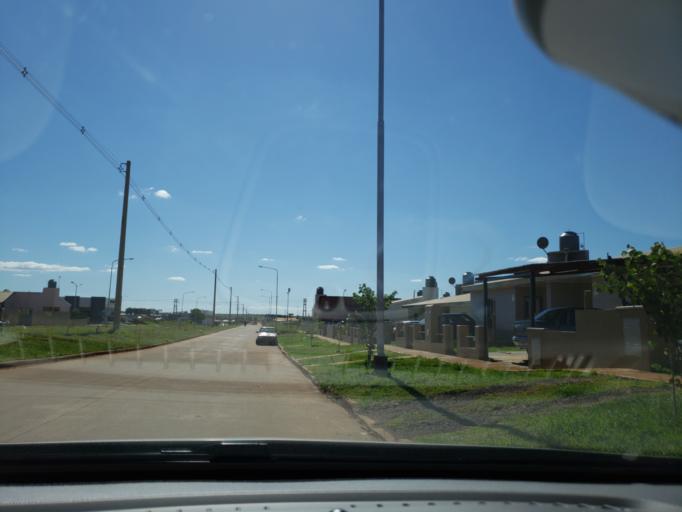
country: AR
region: Misiones
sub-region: Departamento de Capital
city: Posadas
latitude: -27.4084
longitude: -55.9821
